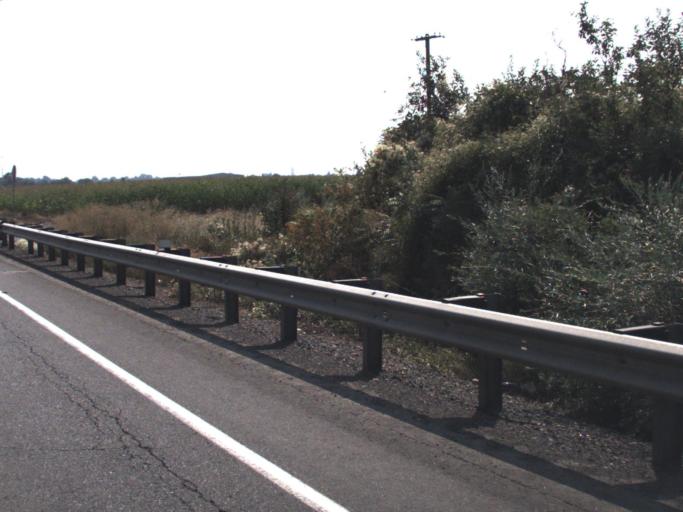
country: US
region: Washington
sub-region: Yakima County
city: Toppenish
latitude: 46.4041
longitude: -120.3146
